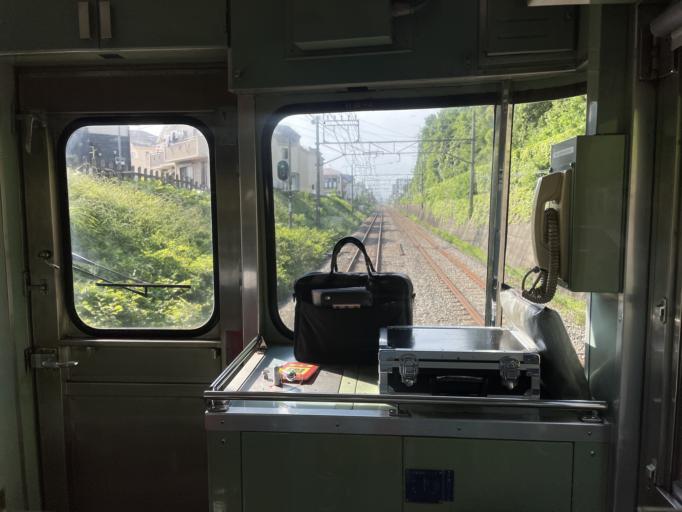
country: JP
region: Tokyo
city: Kokubunji
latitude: 35.7025
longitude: 139.4711
